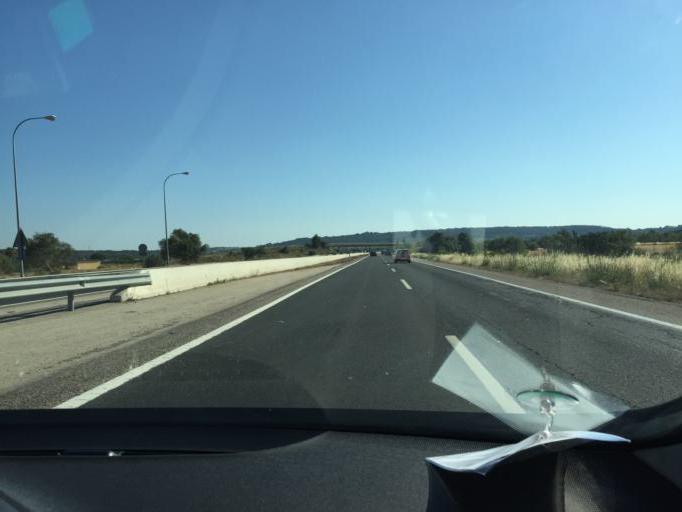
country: ES
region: Balearic Islands
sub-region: Illes Balears
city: Consell
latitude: 39.6533
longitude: 2.7998
